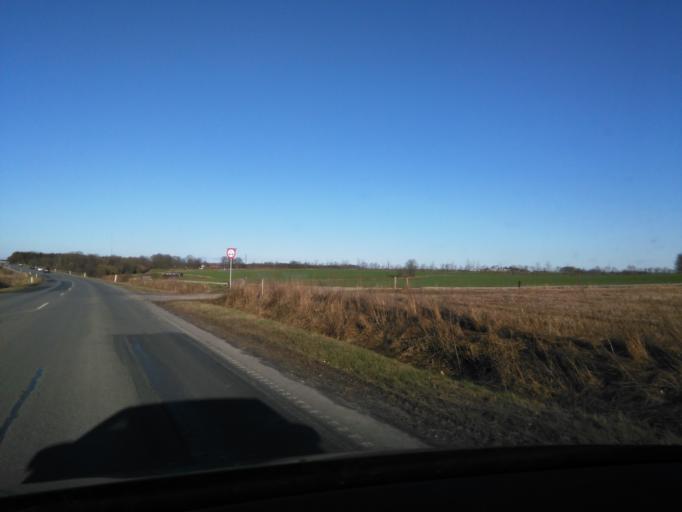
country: DK
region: North Denmark
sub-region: Mariagerfjord Kommune
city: Hobro
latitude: 56.6612
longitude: 9.8043
